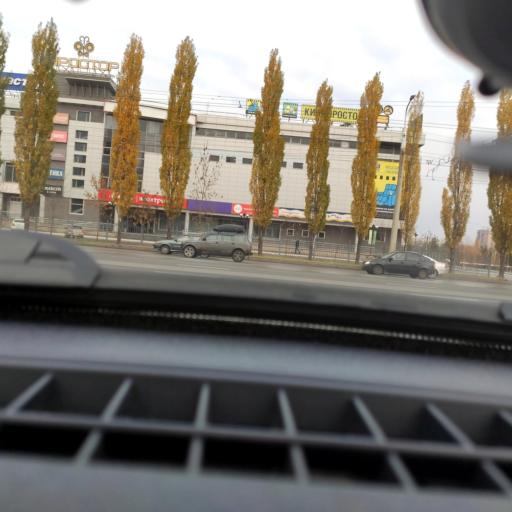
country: RU
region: Bashkortostan
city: Ufa
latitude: 54.7711
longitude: 56.0601
